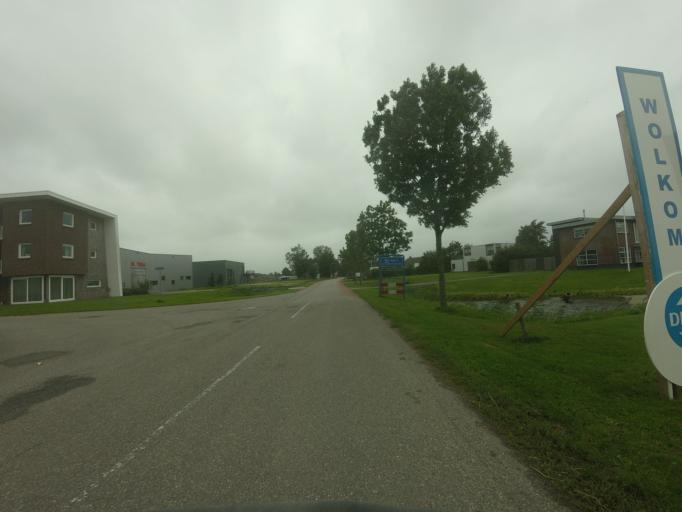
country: NL
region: Friesland
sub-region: Gemeente Ferwerderadiel
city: Ferwert
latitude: 53.3360
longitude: 5.8370
